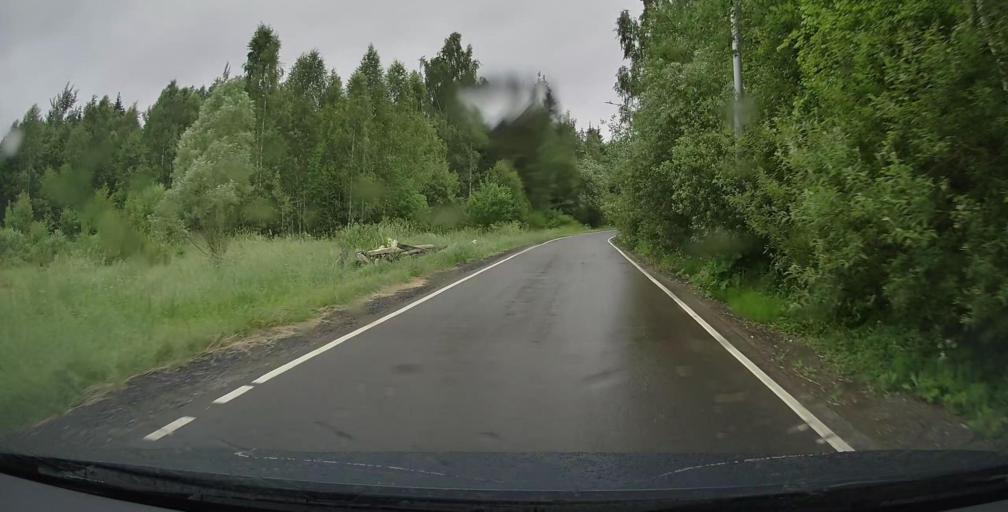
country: RU
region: Moskovskaya
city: Selyatino
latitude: 55.3963
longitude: 37.0090
